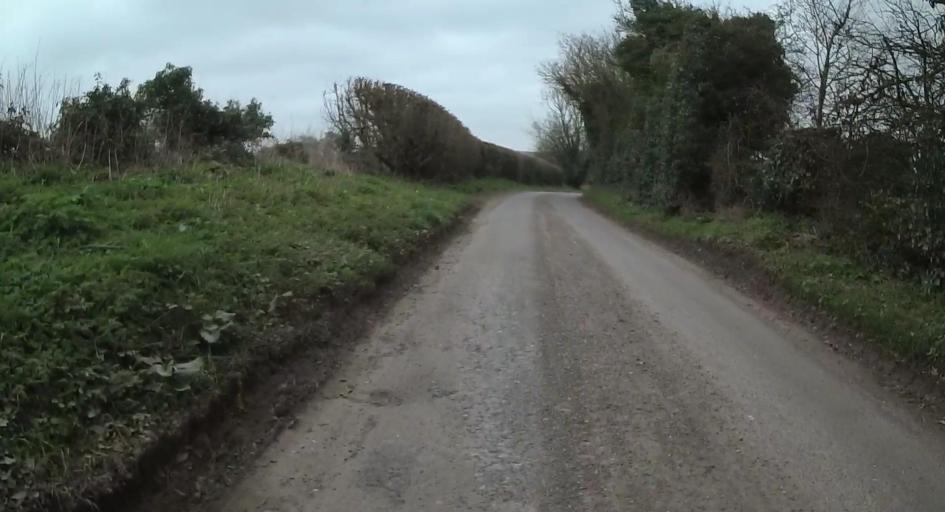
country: GB
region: England
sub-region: Hampshire
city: Four Marks
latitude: 51.1082
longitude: -1.1297
